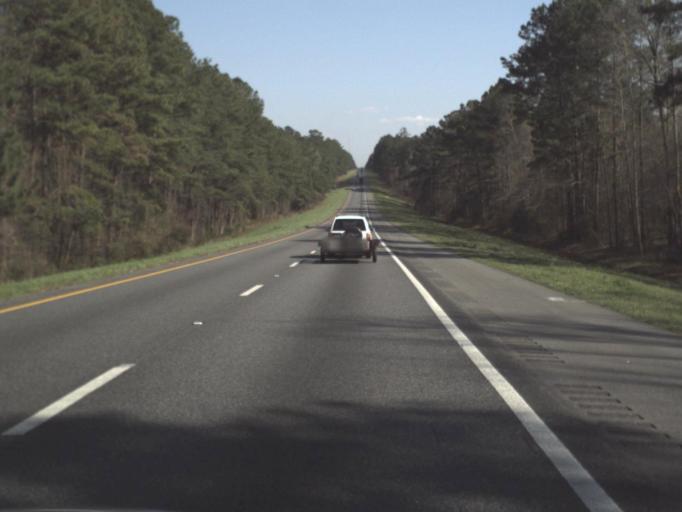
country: US
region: Florida
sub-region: Gadsden County
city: Midway
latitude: 30.5192
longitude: -84.4869
